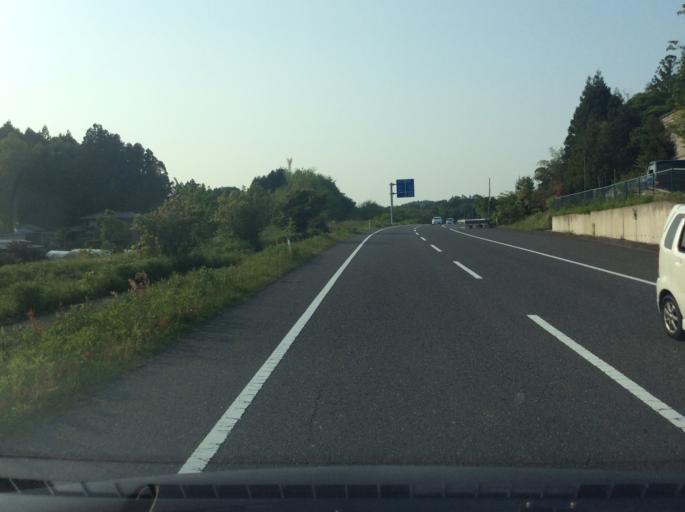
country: JP
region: Fukushima
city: Ishikawa
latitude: 37.2074
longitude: 140.4374
